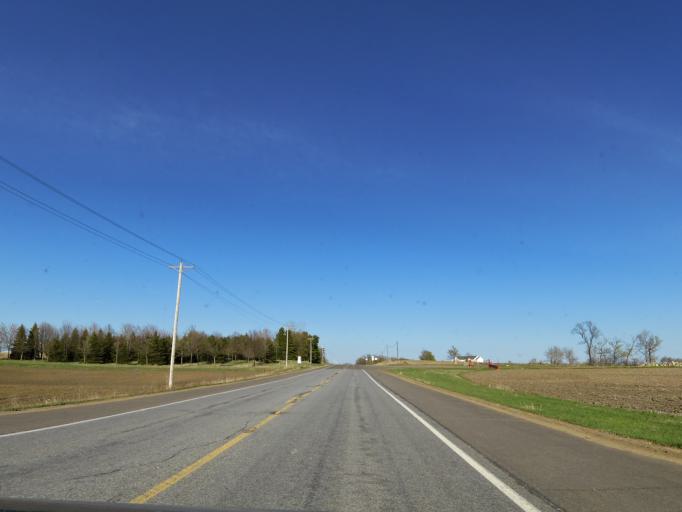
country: US
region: Minnesota
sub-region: Dakota County
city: Lakeville
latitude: 44.6235
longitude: -93.2797
